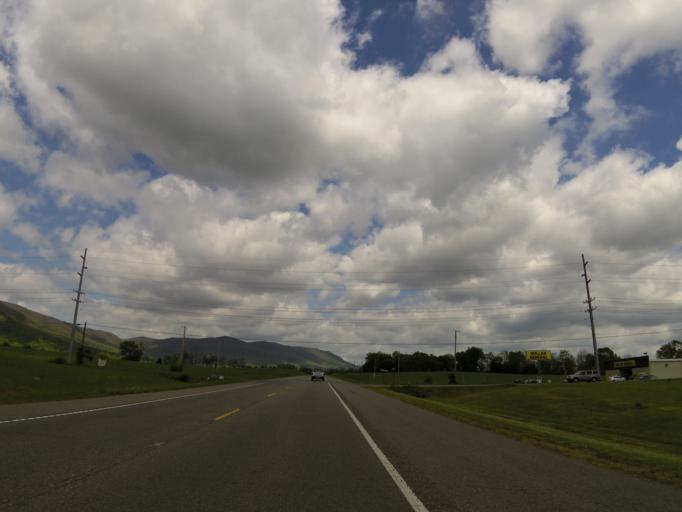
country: US
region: Tennessee
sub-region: Campbell County
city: Fincastle
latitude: 36.4341
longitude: -84.0118
